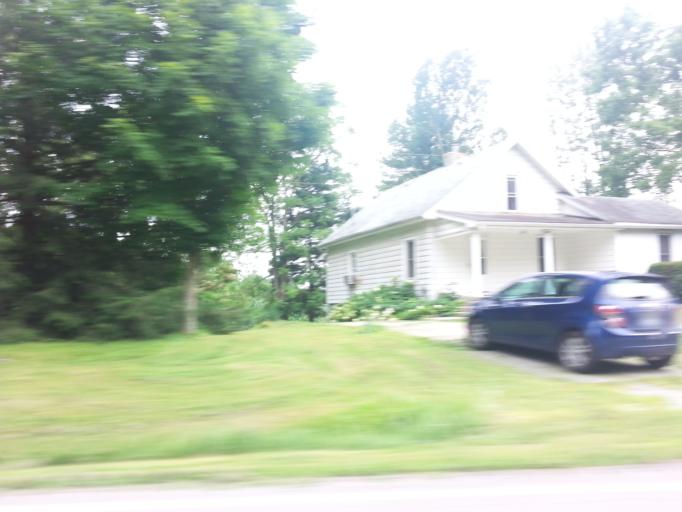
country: US
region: Kentucky
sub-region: Robertson County
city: Mount Olivet
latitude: 38.5327
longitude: -84.0179
